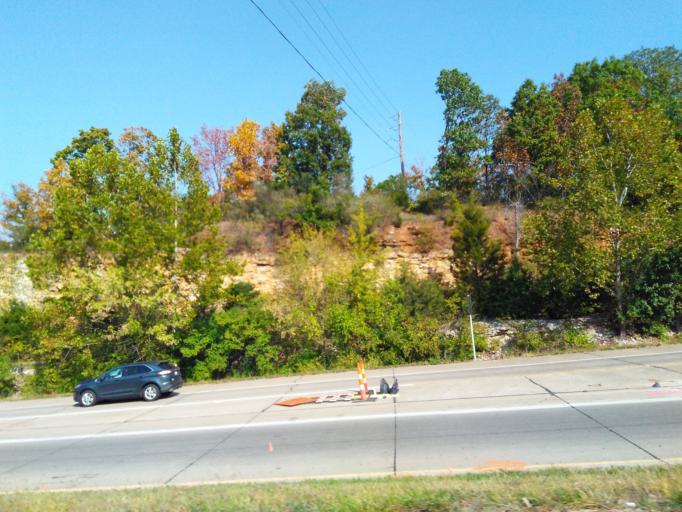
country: US
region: Missouri
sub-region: Saint Louis County
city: Valley Park
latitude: 38.5396
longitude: -90.4856
